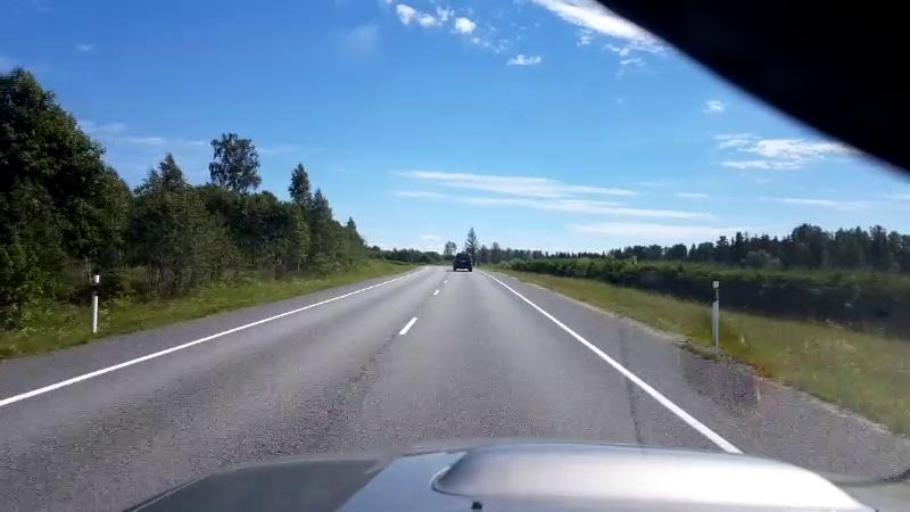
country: EE
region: Jaervamaa
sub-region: Jaerva-Jaani vald
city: Jarva-Jaani
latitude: 59.0211
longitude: 25.9020
